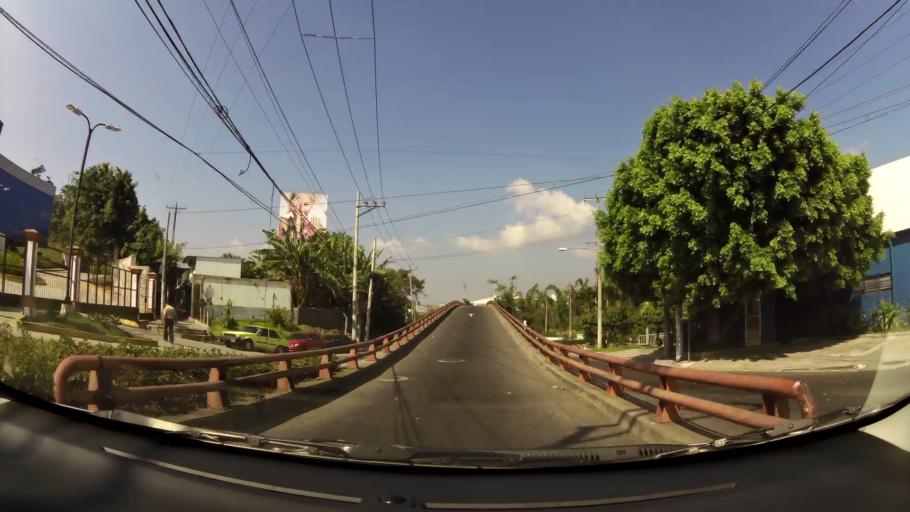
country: SV
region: La Libertad
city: Antiguo Cuscatlan
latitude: 13.6767
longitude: -89.2472
